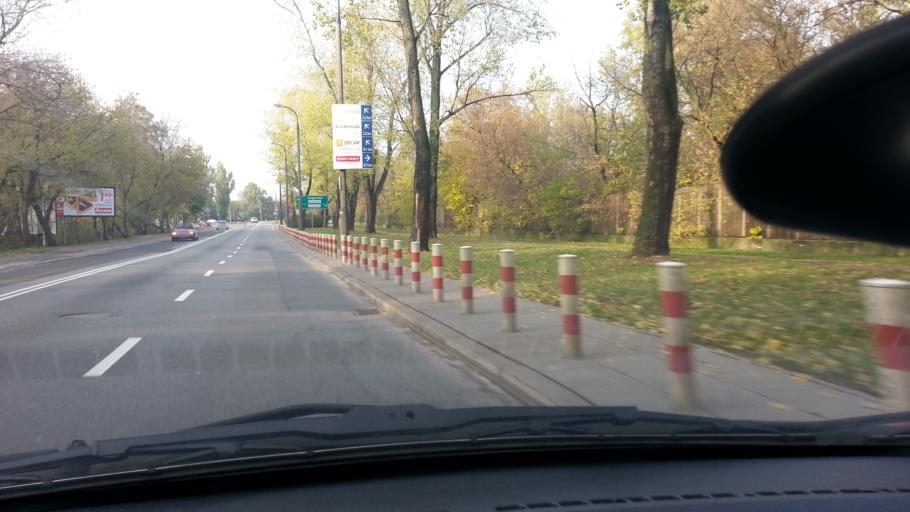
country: PL
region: Masovian Voivodeship
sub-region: Warszawa
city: Praga Polnoc
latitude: 52.2595
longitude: 21.0171
